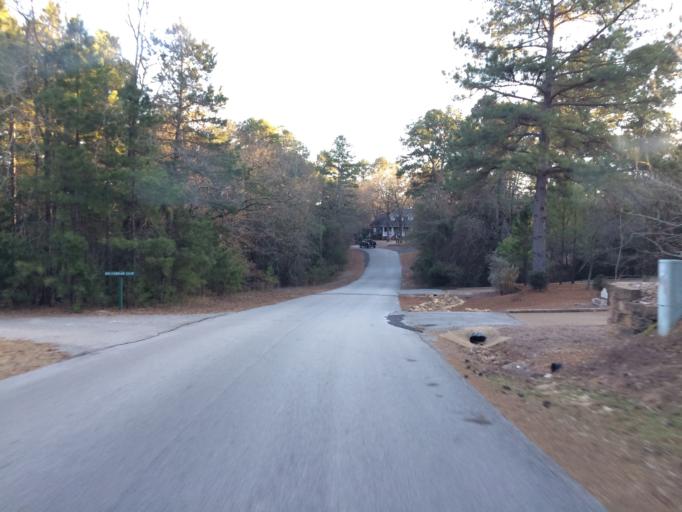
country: US
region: Texas
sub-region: Wood County
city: Hawkins
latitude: 32.7269
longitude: -95.1880
